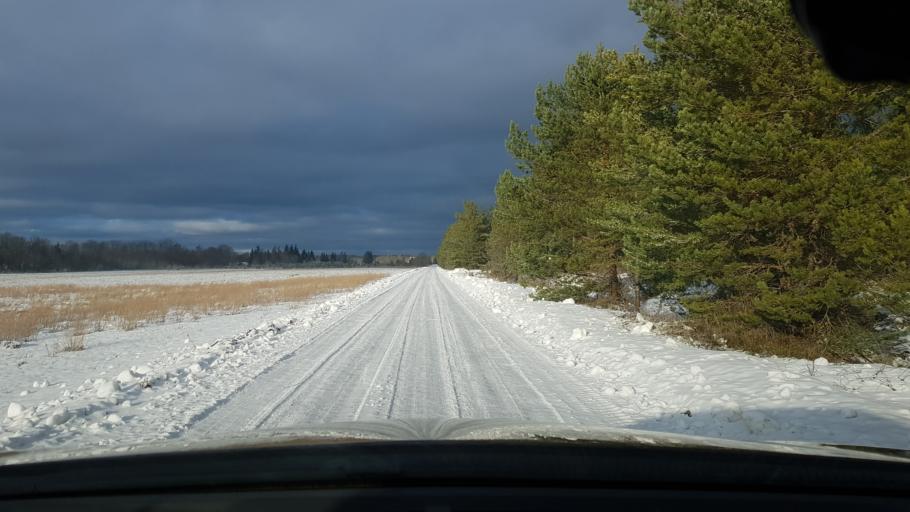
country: EE
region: Harju
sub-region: Keila linn
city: Keila
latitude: 59.2998
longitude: 24.2464
